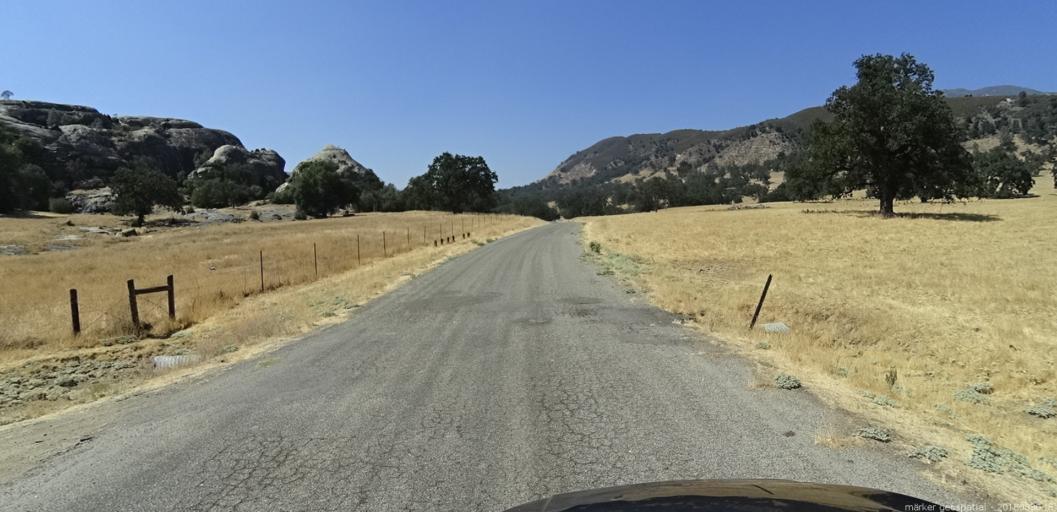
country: US
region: California
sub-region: Monterey County
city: Greenfield
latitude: 36.0842
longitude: -121.4008
